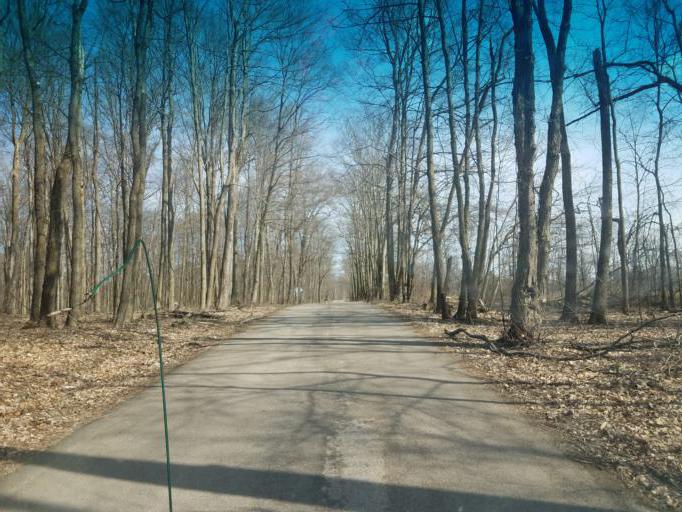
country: US
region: Ohio
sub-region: Richland County
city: Lincoln Heights
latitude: 40.8368
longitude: -82.5039
